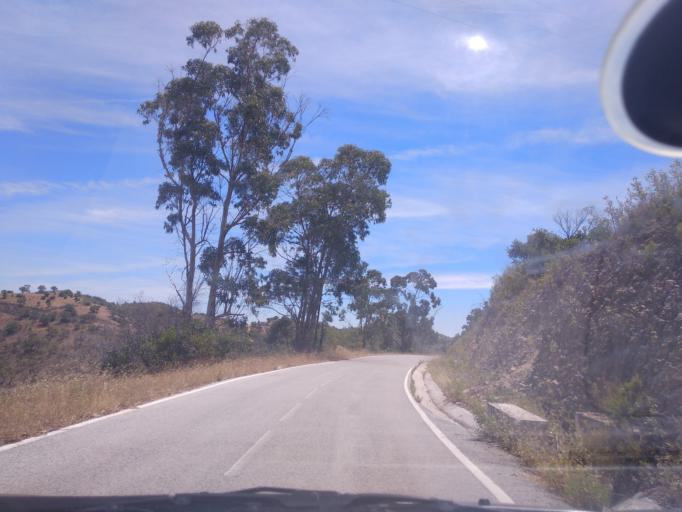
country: PT
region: Faro
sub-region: Sao Bras de Alportel
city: Sao Bras de Alportel
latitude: 37.2017
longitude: -7.8080
